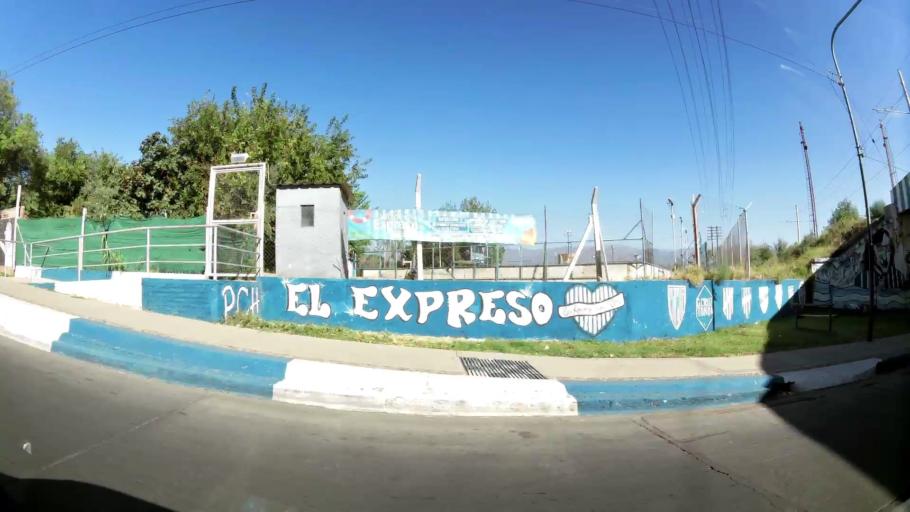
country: AR
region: Mendoza
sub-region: Departamento de Godoy Cruz
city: Godoy Cruz
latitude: -32.9205
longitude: -68.8414
